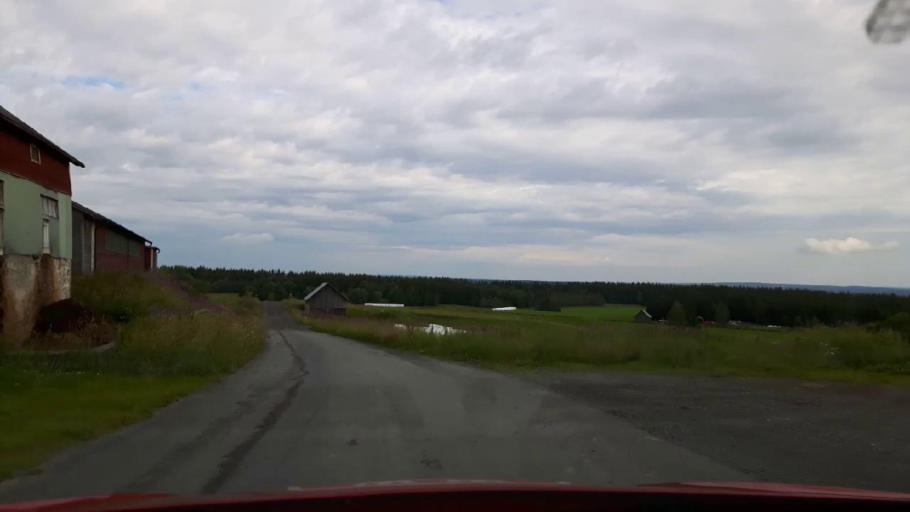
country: SE
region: Jaemtland
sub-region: OEstersunds Kommun
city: Lit
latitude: 63.3796
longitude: 15.1940
